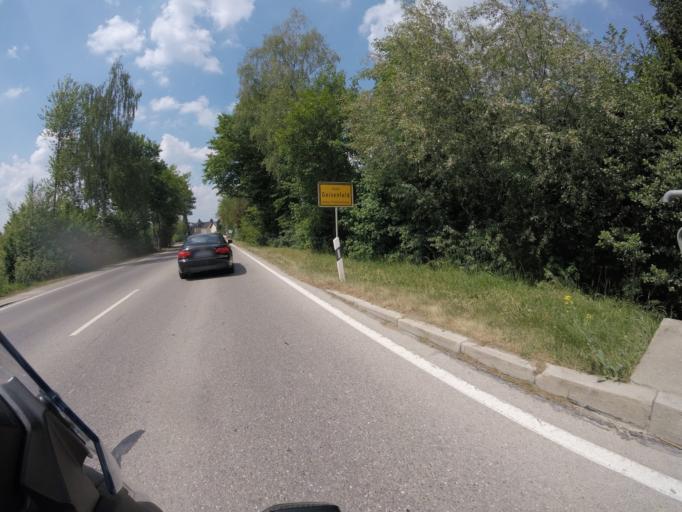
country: DE
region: Bavaria
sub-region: Upper Bavaria
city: Geisenfeld
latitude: 48.6873
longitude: 11.6239
